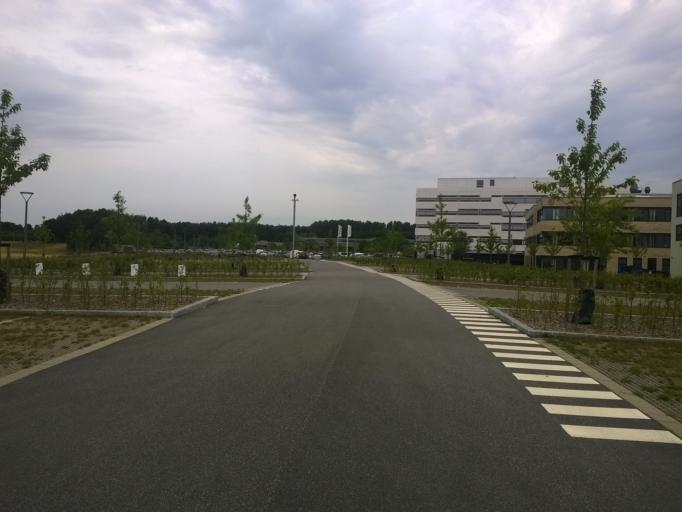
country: DK
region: Capital Region
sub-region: Ballerup Kommune
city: Ballerup
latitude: 55.7309
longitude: 12.3793
